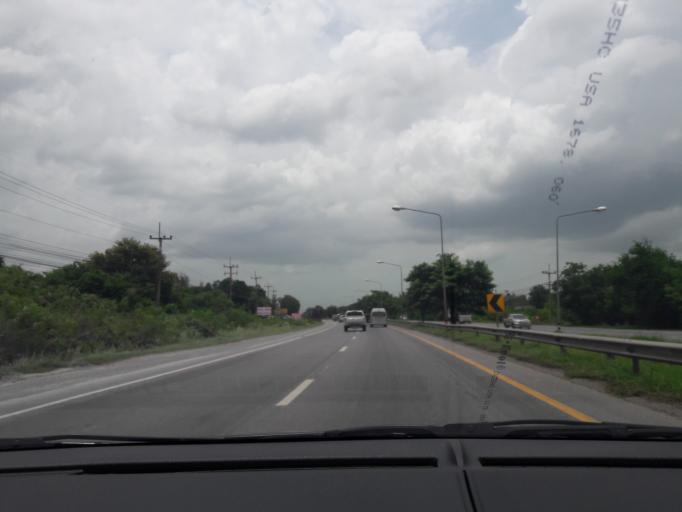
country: TH
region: Nakhon Ratchasima
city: Chaloem Phra Kiat
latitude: 15.0714
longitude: 102.2113
